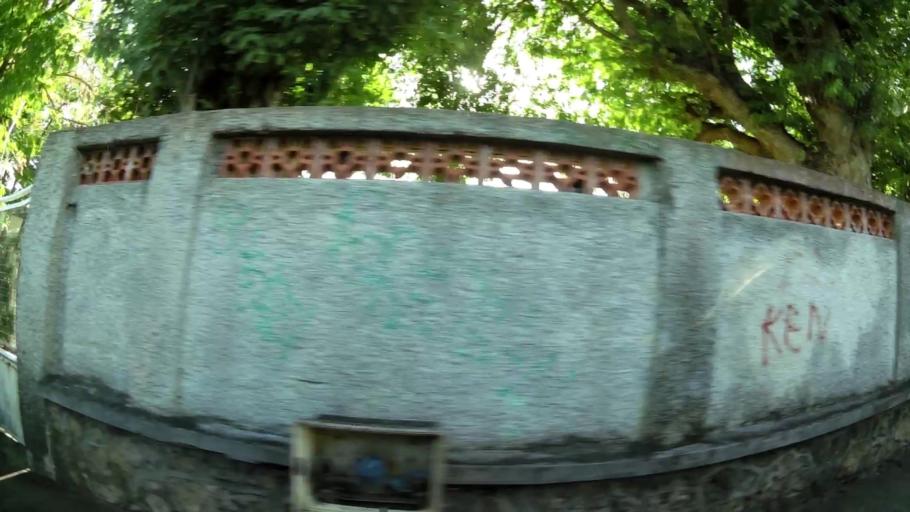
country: GP
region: Guadeloupe
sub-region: Guadeloupe
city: Le Gosier
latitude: 16.2043
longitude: -61.4794
